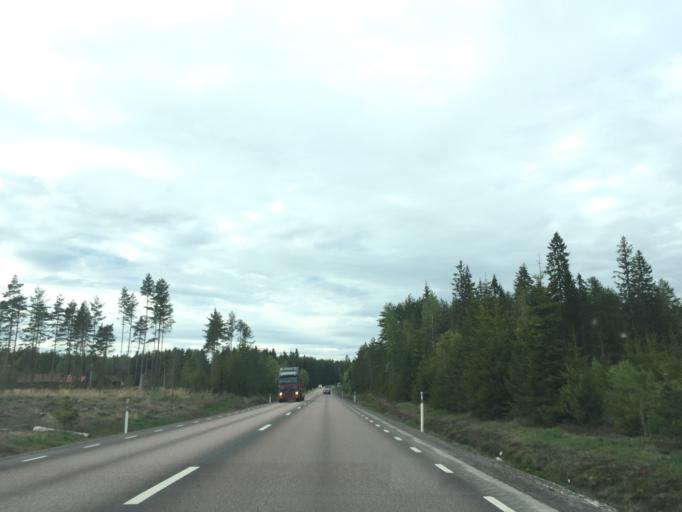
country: SE
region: Vaermland
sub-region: Eda Kommun
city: Charlottenberg
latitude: 59.8934
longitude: 12.2798
